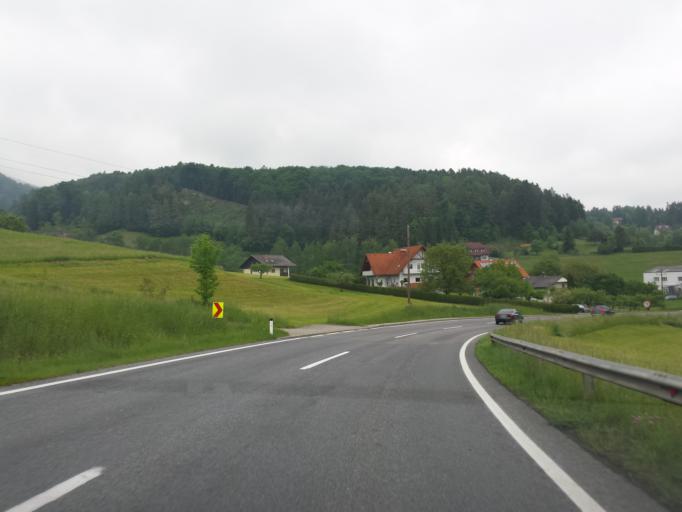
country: AT
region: Styria
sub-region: Politischer Bezirk Weiz
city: Puch bei Weiz
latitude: 47.2355
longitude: 15.6833
